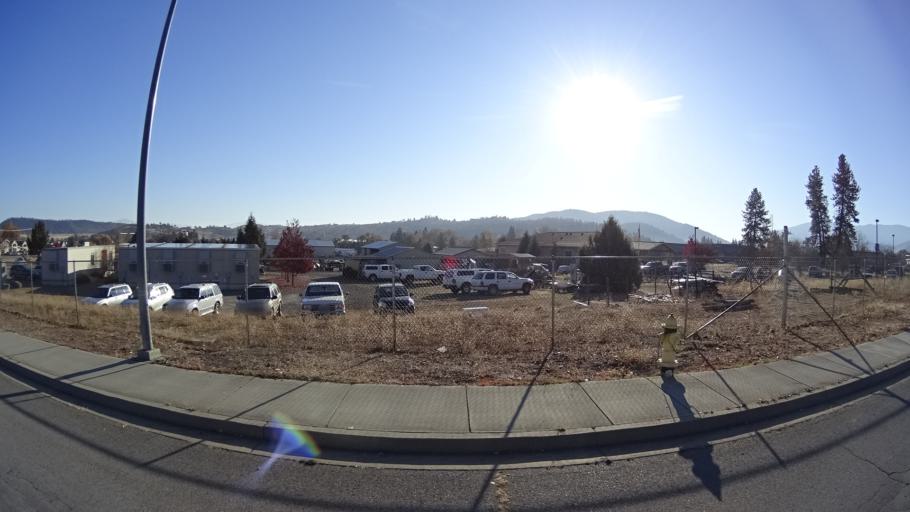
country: US
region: California
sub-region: Siskiyou County
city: Yreka
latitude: 41.7083
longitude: -122.6454
